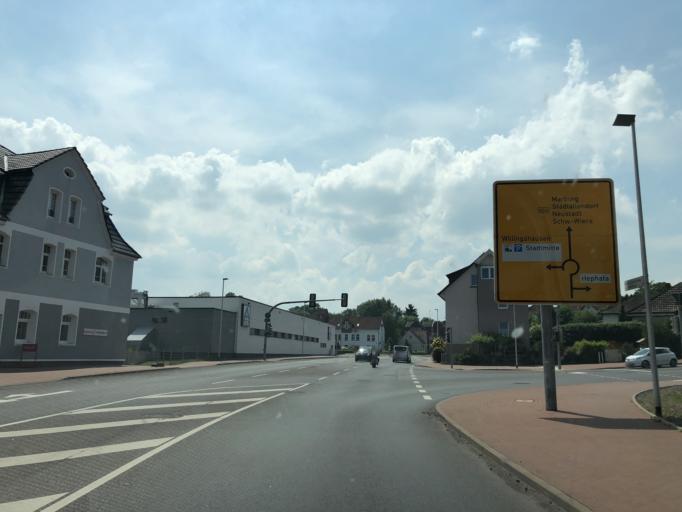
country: DE
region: Hesse
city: Schwalmstadt
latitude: 50.9122
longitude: 9.1818
